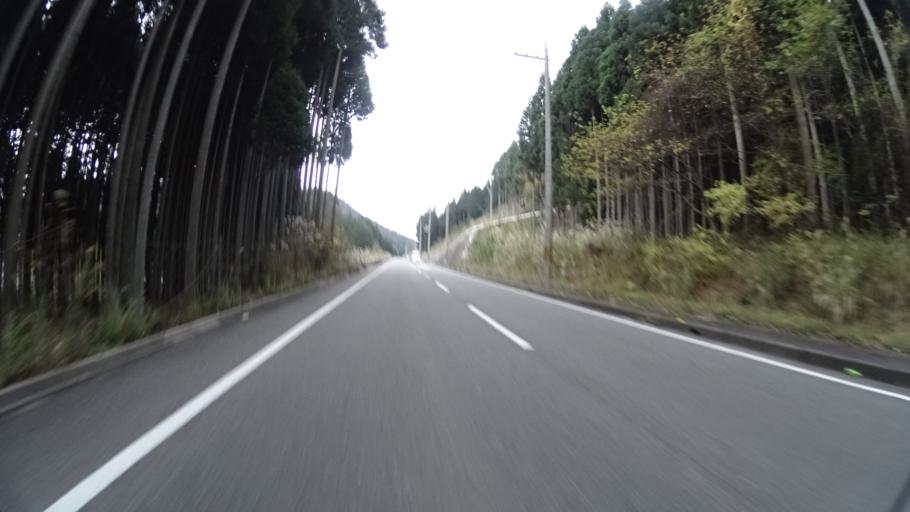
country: JP
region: Kyoto
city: Kameoka
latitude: 35.0657
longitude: 135.4065
